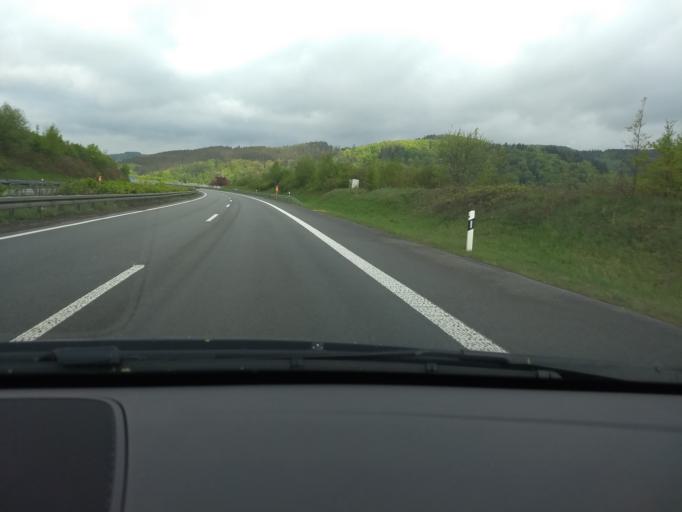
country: DE
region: North Rhine-Westphalia
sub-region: Regierungsbezirk Arnsberg
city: Arnsberg
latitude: 51.3893
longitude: 8.1139
